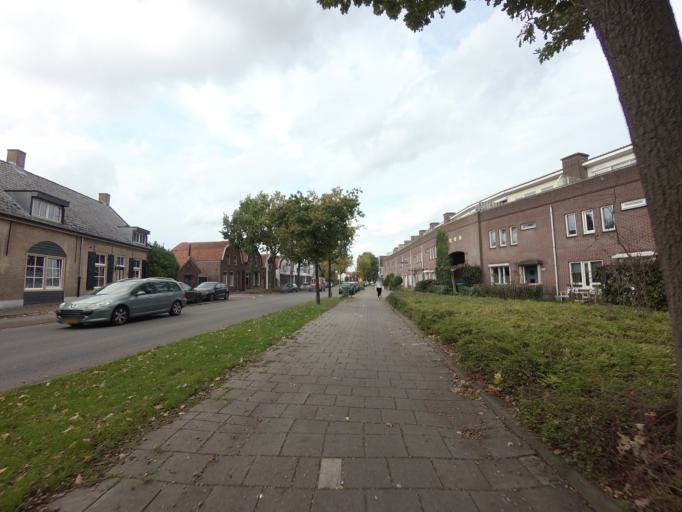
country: NL
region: North Brabant
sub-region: Gemeente Breda
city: Breda
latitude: 51.5704
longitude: 4.7431
